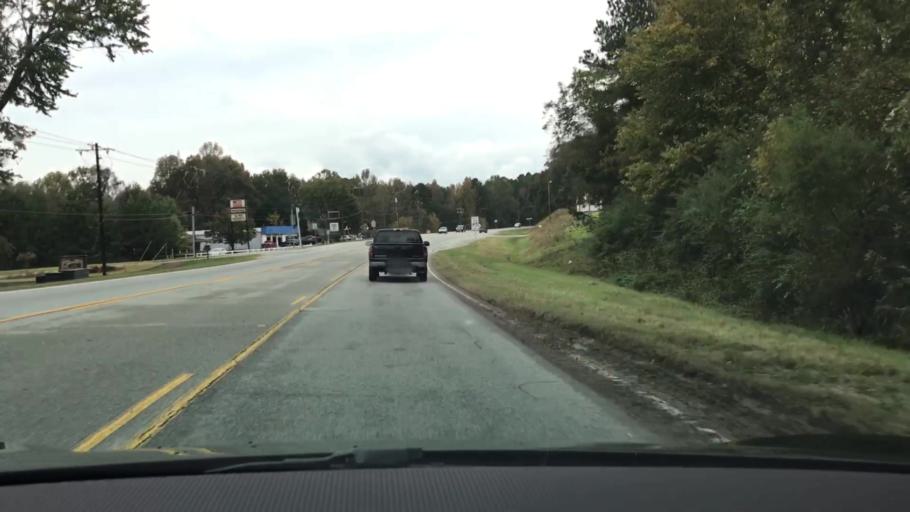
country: US
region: Georgia
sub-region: Greene County
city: Greensboro
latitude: 33.5619
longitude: -83.1844
